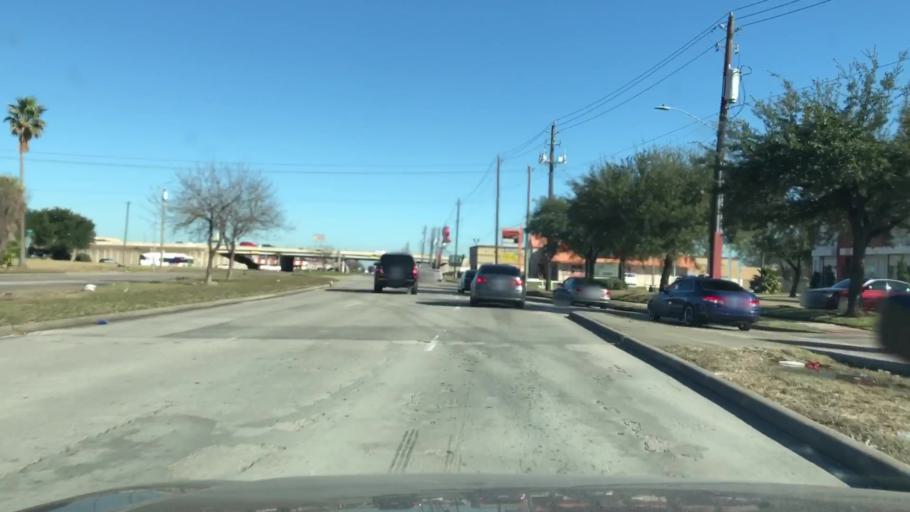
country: US
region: Texas
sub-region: Harris County
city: Aldine
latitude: 29.8698
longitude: -95.4104
